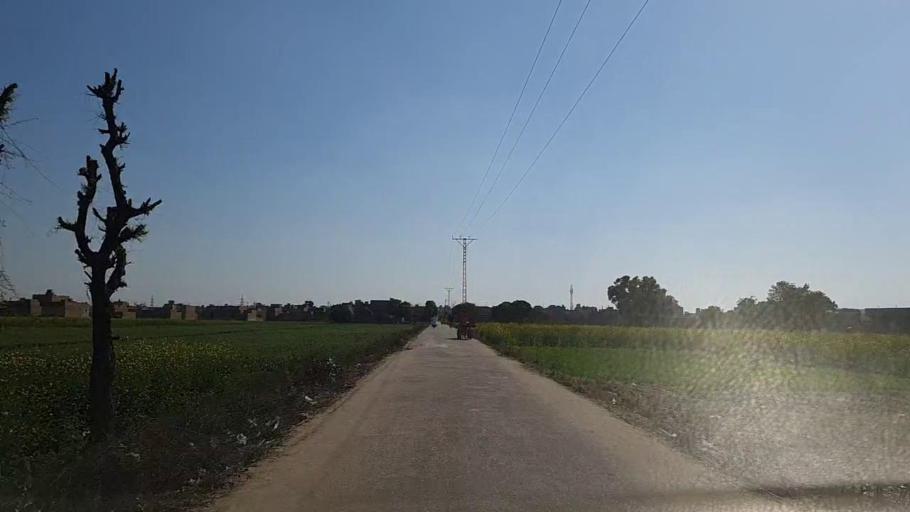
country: PK
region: Sindh
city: Nawabshah
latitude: 26.2587
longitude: 68.4243
